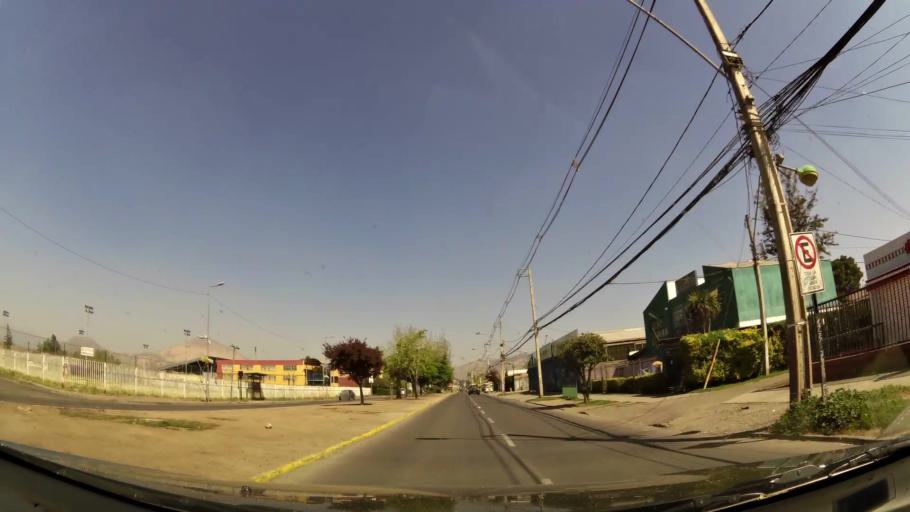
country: CL
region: Santiago Metropolitan
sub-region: Provincia de Santiago
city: Lo Prado
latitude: -33.3601
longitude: -70.7294
